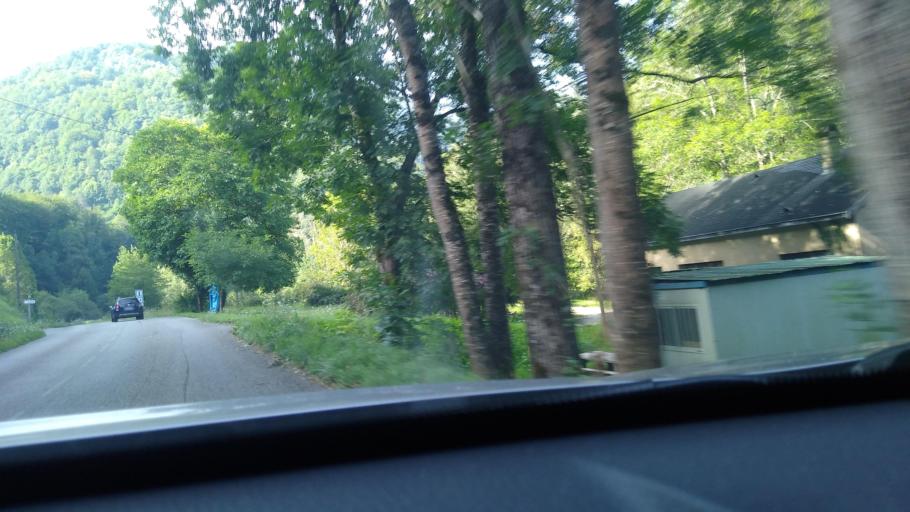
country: FR
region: Midi-Pyrenees
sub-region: Departement de l'Ariege
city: Saint-Girons
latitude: 42.8458
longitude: 1.1921
